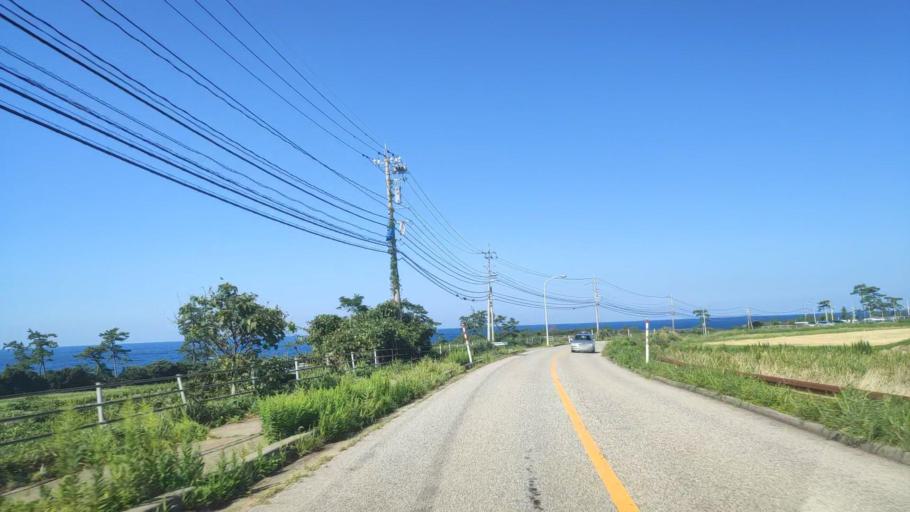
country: JP
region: Ishikawa
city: Hakui
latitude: 37.0534
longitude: 136.7279
